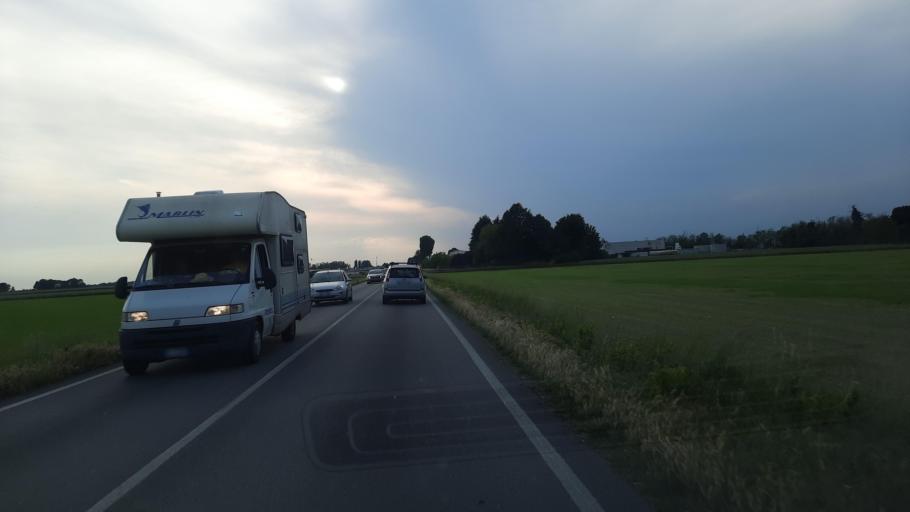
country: IT
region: Lombardy
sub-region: Provincia di Pavia
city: Carbonara al Ticino
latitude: 45.1588
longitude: 9.0825
